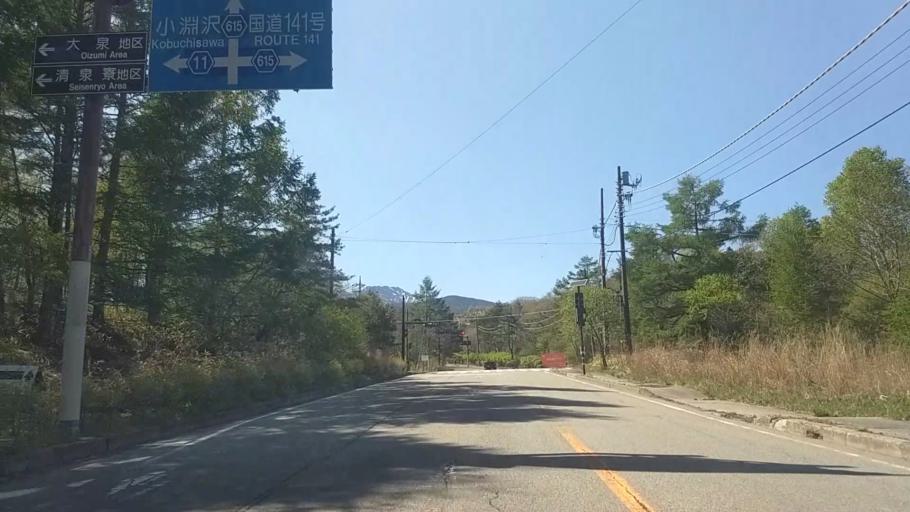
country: JP
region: Yamanashi
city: Nirasaki
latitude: 35.9342
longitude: 138.4250
